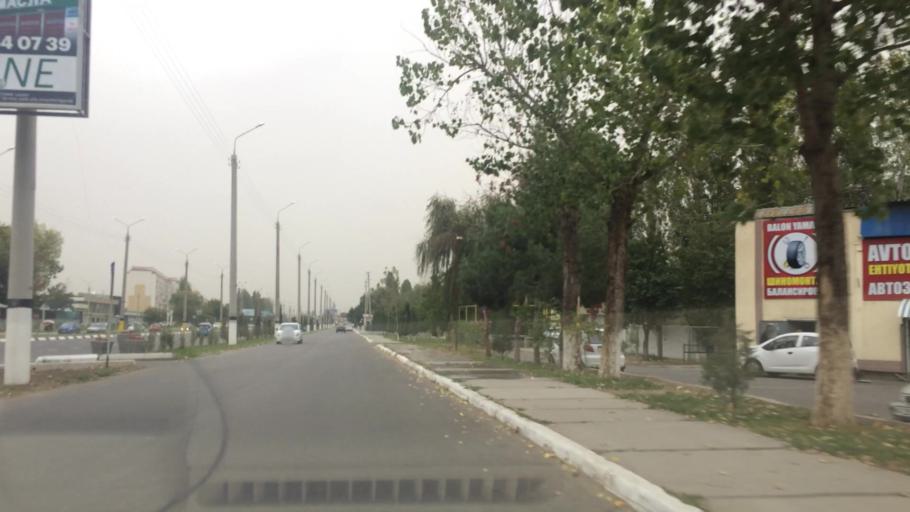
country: UZ
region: Toshkent
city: Salor
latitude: 41.3128
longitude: 69.3497
